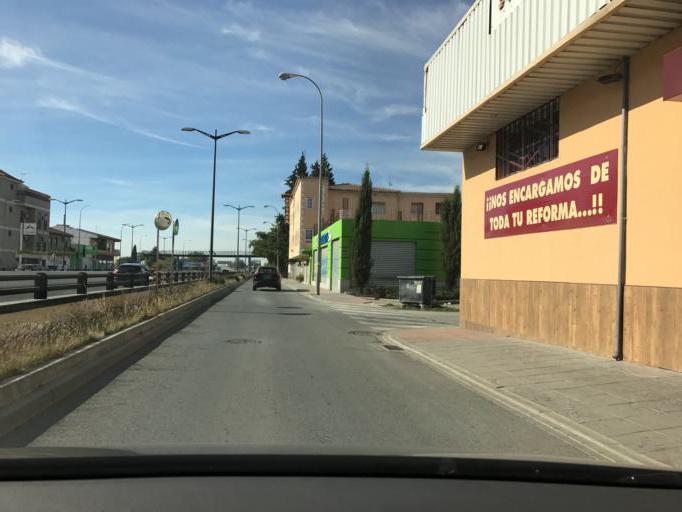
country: ES
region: Andalusia
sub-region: Provincia de Granada
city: Atarfe
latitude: 37.1926
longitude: -3.7158
